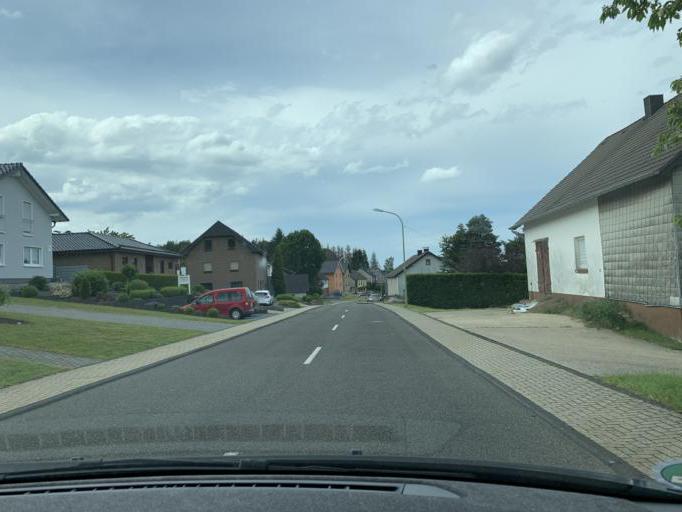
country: DE
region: North Rhine-Westphalia
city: Heimbach
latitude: 50.6676
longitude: 6.4108
